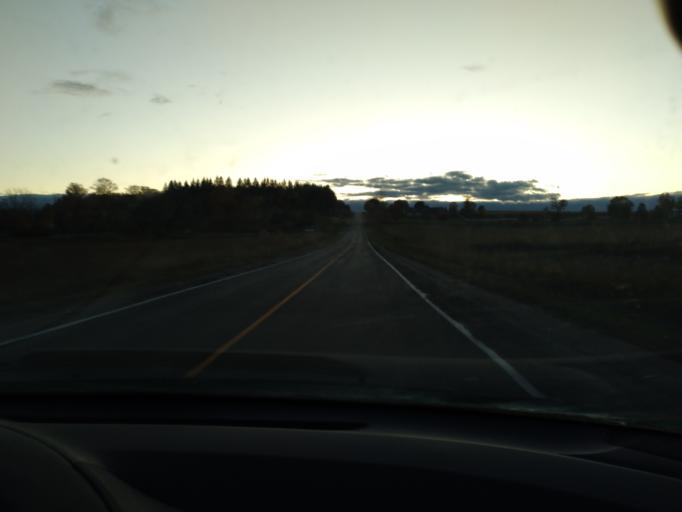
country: CA
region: Ontario
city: Innisfil
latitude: 44.2431
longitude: -79.6398
